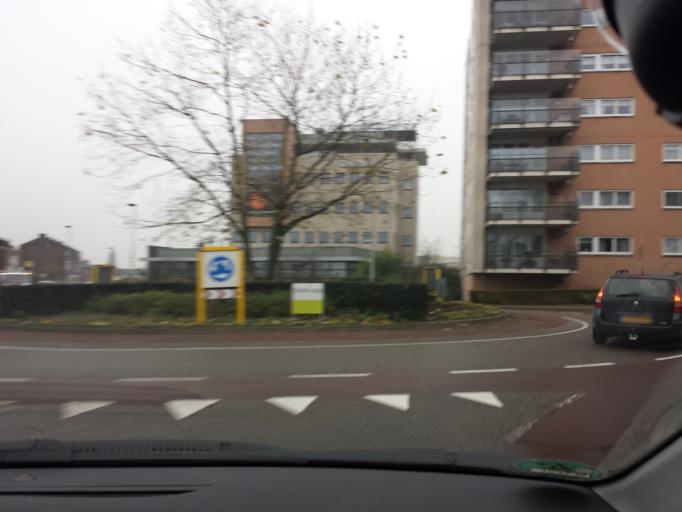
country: NL
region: Limburg
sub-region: Gemeente Heerlen
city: Heerlen
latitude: 50.9057
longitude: 6.0212
